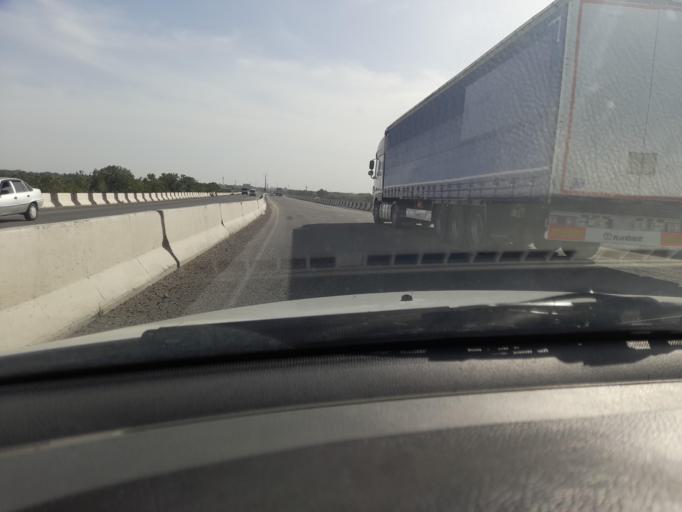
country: UZ
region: Samarqand
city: Kattaqo'rg'on
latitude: 39.9318
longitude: 66.3642
